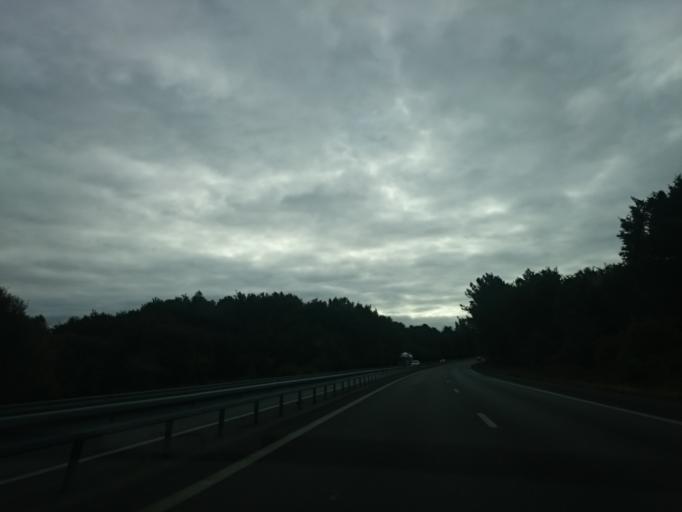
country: FR
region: Brittany
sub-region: Departement du Morbihan
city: Landevant
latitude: 47.7533
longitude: -3.1116
